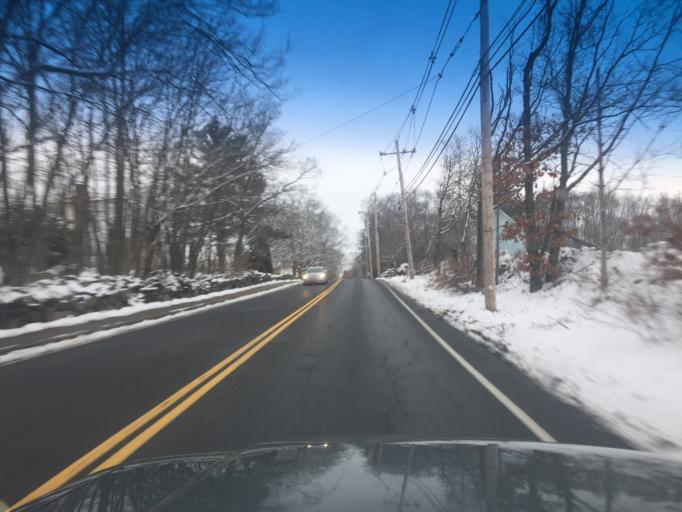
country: US
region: Massachusetts
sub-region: Middlesex County
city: Holliston
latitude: 42.1974
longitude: -71.4194
